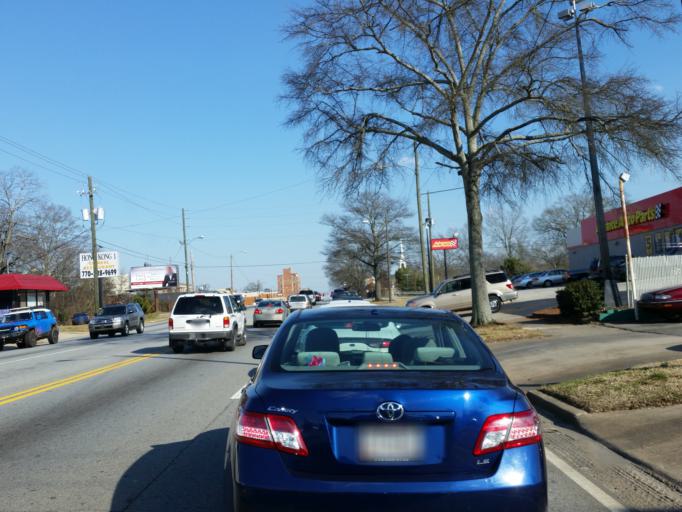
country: US
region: Georgia
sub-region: Spalding County
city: Griffin
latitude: 33.2472
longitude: -84.2683
